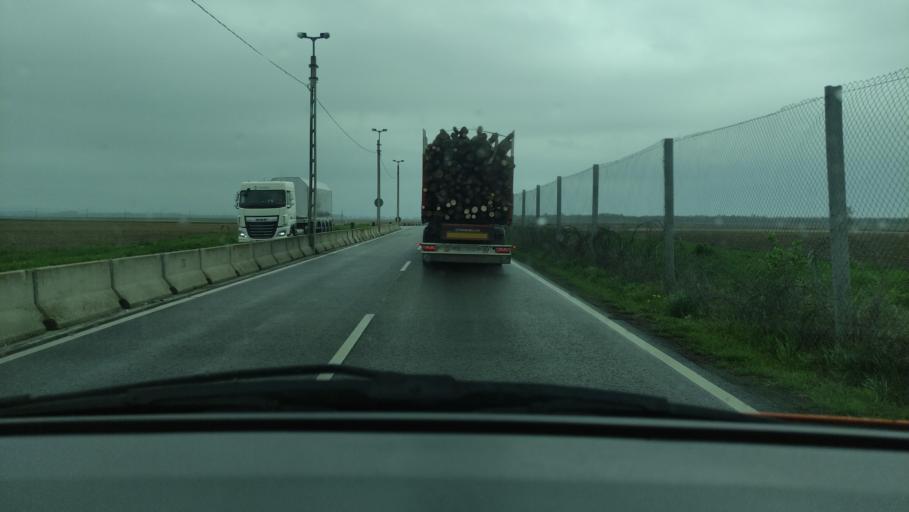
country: HU
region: Baranya
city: Mohacs
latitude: 45.9069
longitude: 18.6597
